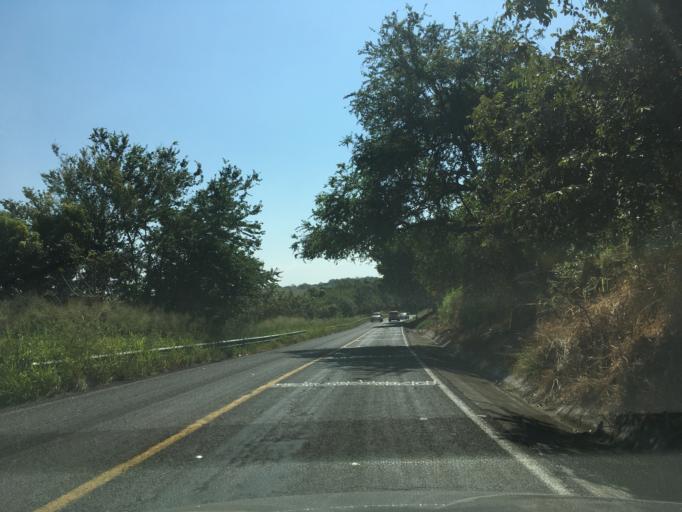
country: MX
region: Michoacan
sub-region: Gabriel Zamora
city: Lombardia
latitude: 19.2296
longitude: -102.0483
